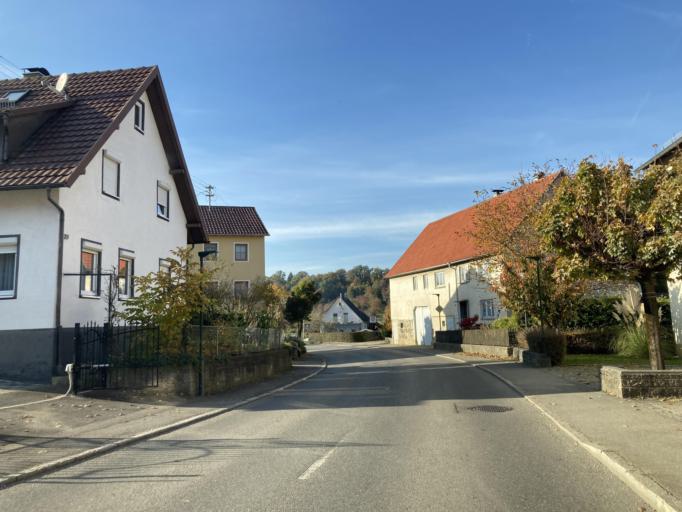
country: DE
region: Baden-Wuerttemberg
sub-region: Tuebingen Region
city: Nehren
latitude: 48.4148
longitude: 9.1041
